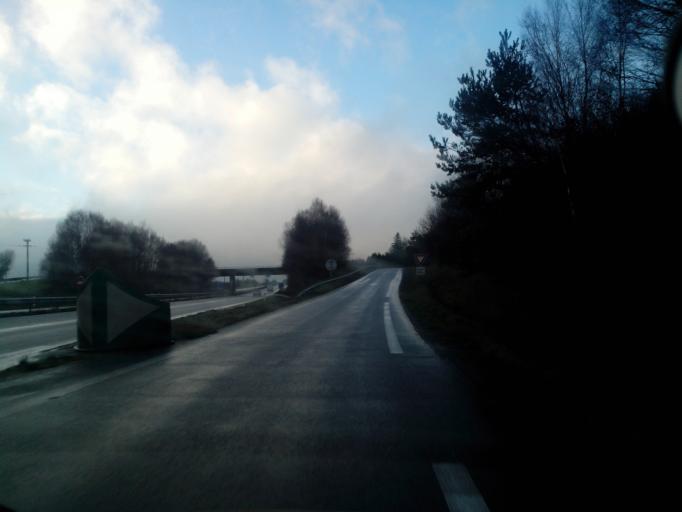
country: FR
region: Brittany
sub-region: Departement des Cotes-d'Armor
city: Merdrignac
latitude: 48.1871
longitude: -2.4227
